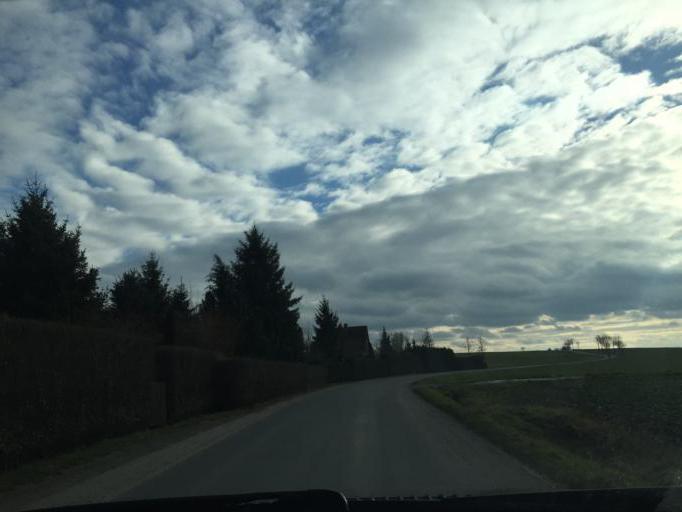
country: DE
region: Saxony
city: Ebersbach
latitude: 51.2261
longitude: 13.6630
